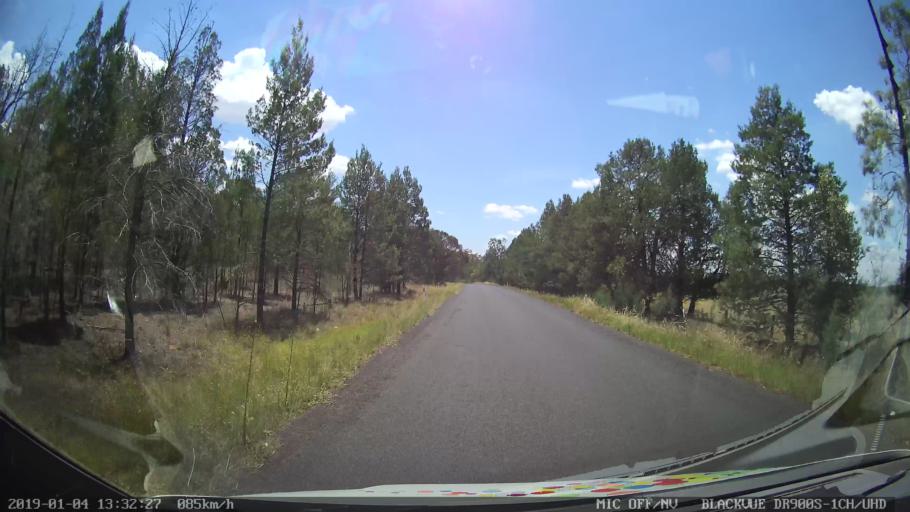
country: AU
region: New South Wales
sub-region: Dubbo Municipality
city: Eulomogo
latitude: -32.6093
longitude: 148.5481
